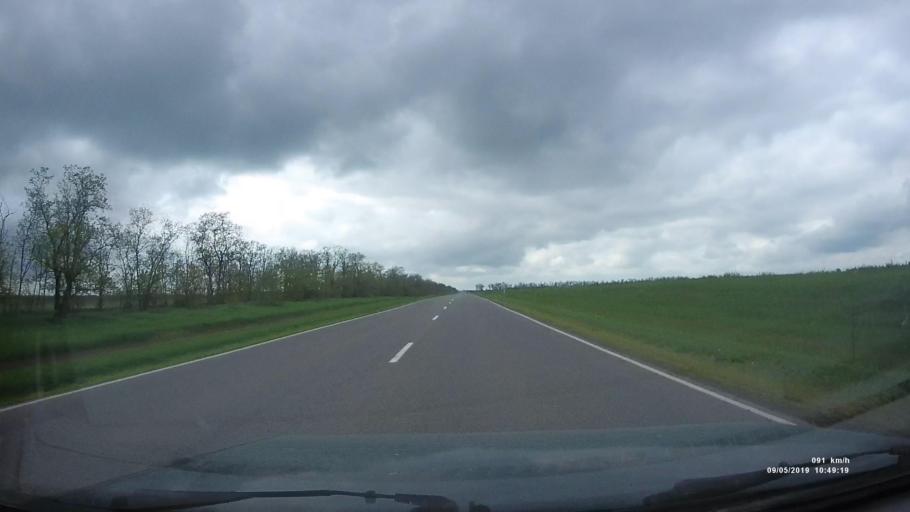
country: RU
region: Rostov
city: Peshkovo
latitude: 46.9440
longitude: 39.3555
